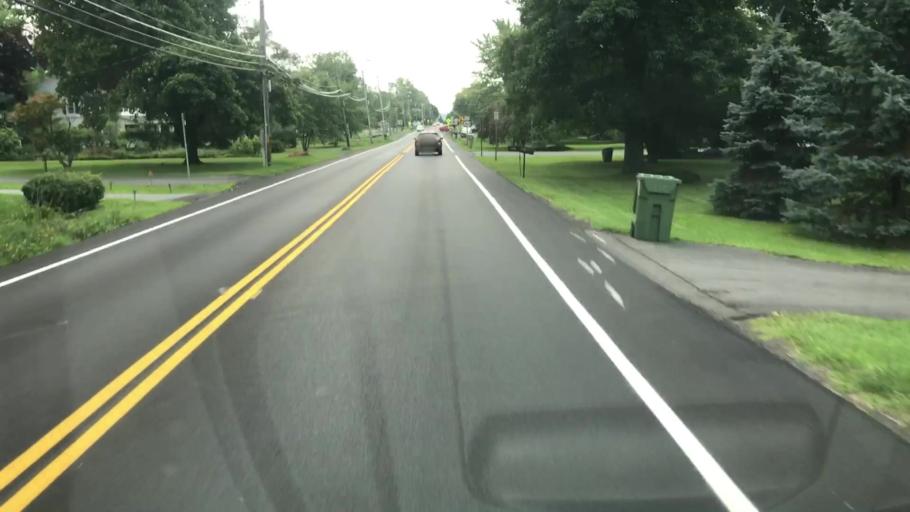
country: US
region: New York
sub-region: Cayuga County
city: Melrose Park
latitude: 42.9081
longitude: -76.5396
